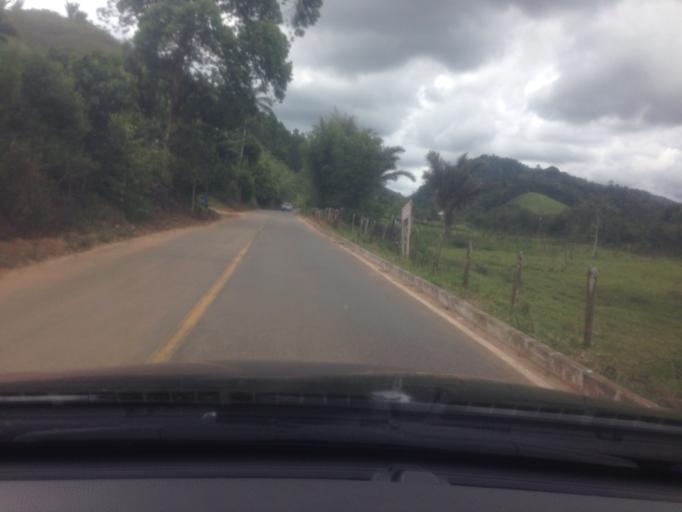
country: BR
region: Espirito Santo
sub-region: Guarapari
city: Guarapari
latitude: -20.5715
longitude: -40.5447
